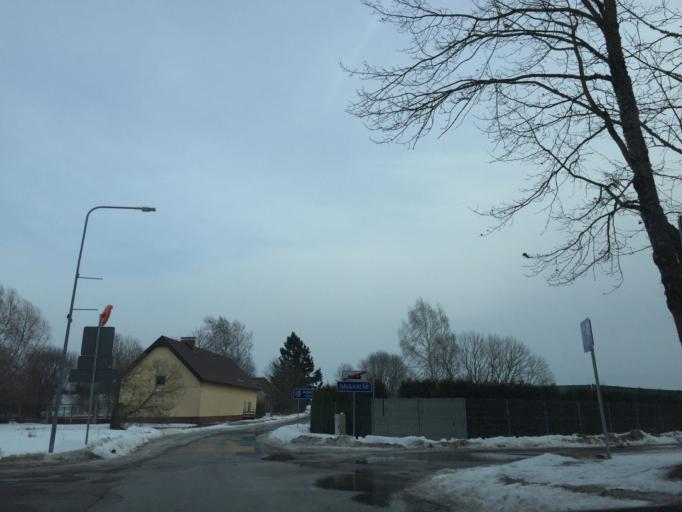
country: LV
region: Ikskile
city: Ikskile
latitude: 56.8458
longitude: 24.4418
